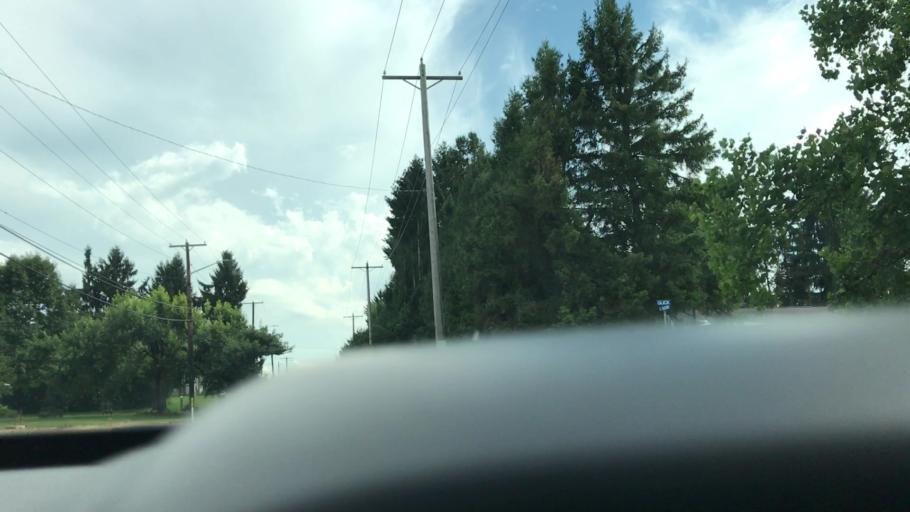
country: US
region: Ohio
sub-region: Stark County
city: Brewster
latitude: 40.7232
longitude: -81.5970
